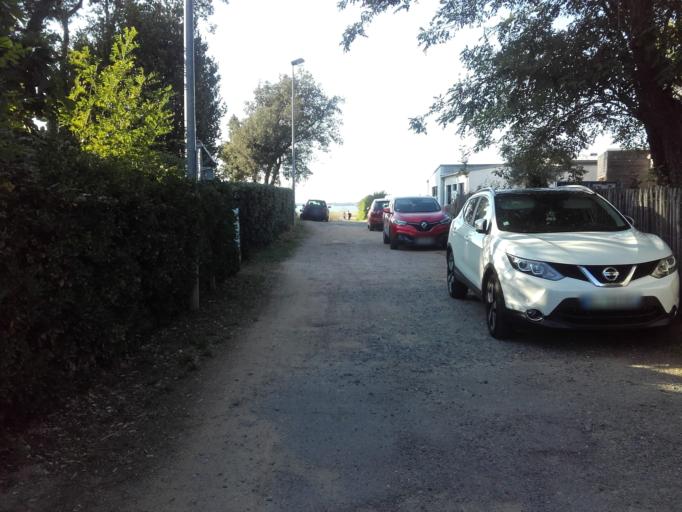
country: FR
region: Pays de la Loire
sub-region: Departement de la Loire-Atlantique
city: Saint-Brevin-les-Pins
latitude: 47.2359
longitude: -2.1741
